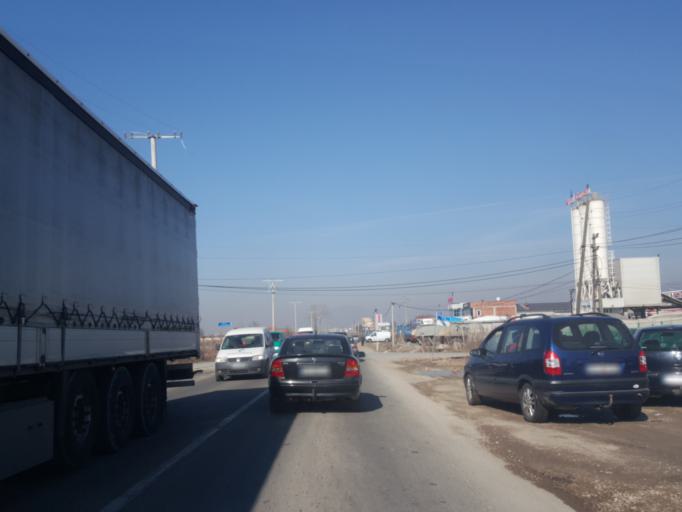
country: XK
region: Mitrovica
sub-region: Vushtrri
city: Vushtrri
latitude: 42.7993
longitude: 20.9965
